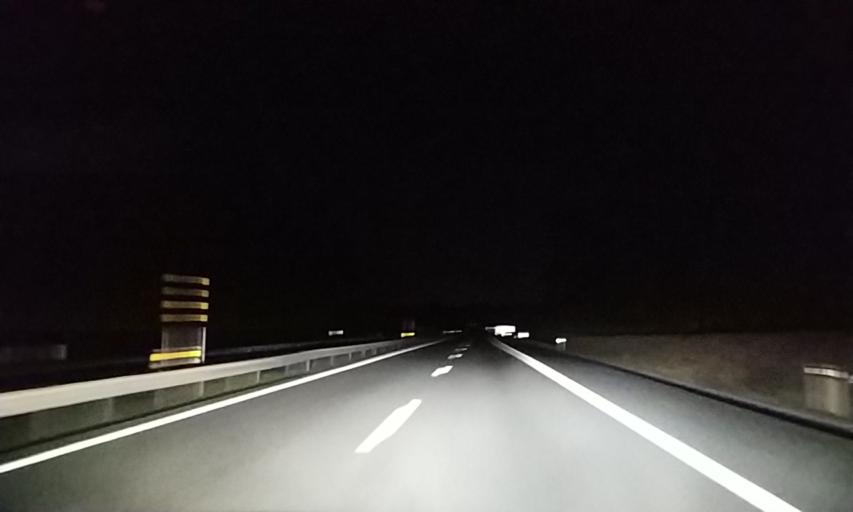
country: PT
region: Aveiro
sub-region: Albergaria-A-Velha
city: Albergaria-a-Velha
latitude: 40.6657
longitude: -8.5153
